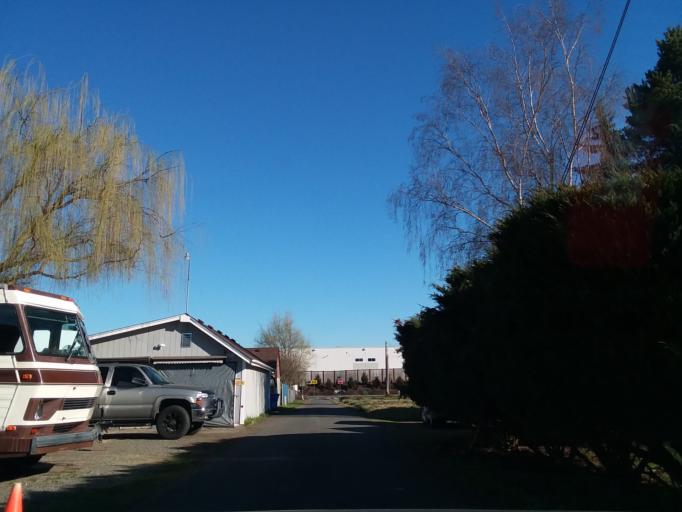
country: US
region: Washington
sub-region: Pierce County
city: Fife
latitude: 47.2453
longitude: -122.3642
